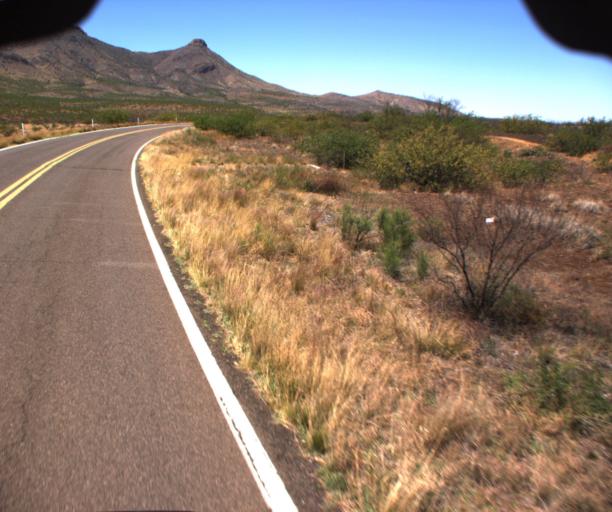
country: US
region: Arizona
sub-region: Cochise County
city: Douglas
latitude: 31.4592
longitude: -109.3763
